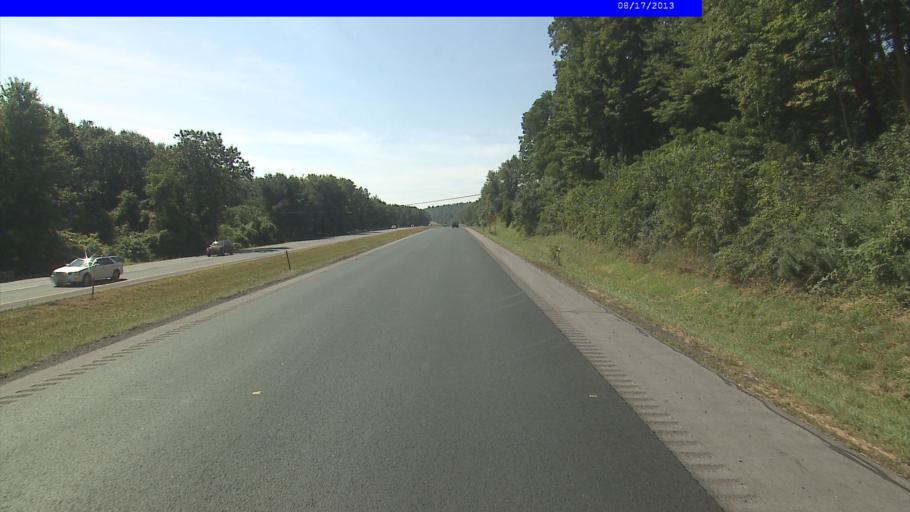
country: US
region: Vermont
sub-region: Windham County
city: Bellows Falls
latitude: 43.0550
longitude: -72.4705
